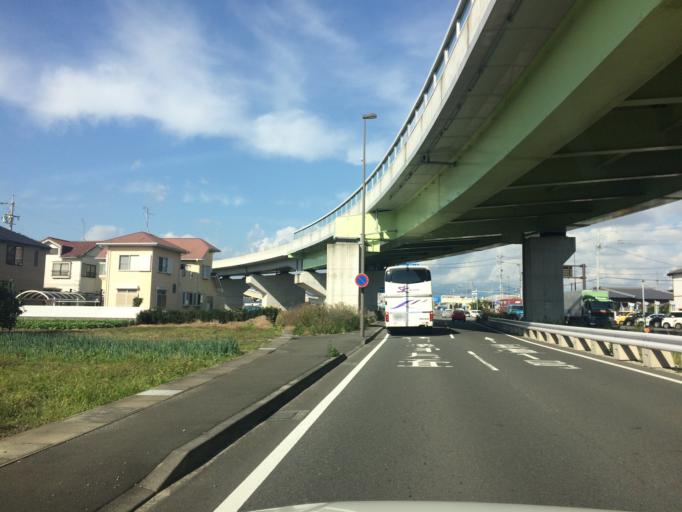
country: JP
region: Shizuoka
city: Shizuoka-shi
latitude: 34.9390
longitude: 138.3972
